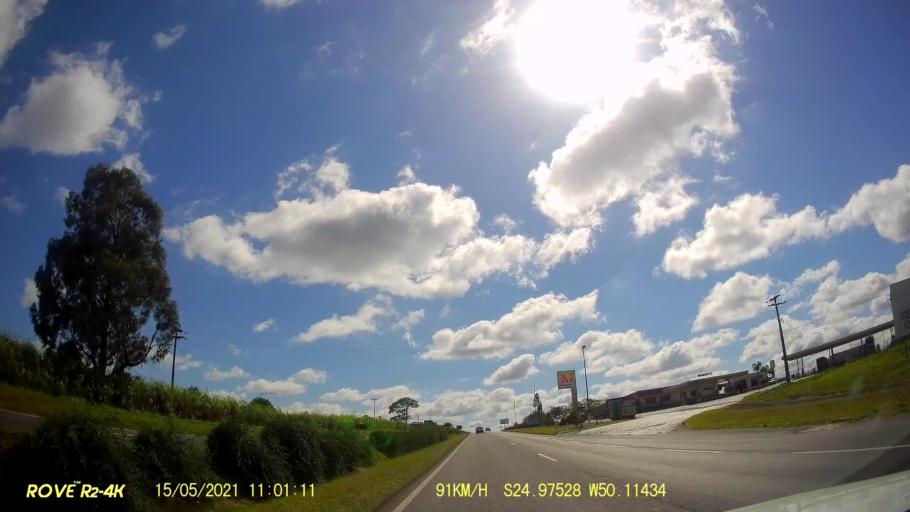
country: BR
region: Parana
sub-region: Carambei
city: Carambei
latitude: -24.9753
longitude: -50.1145
